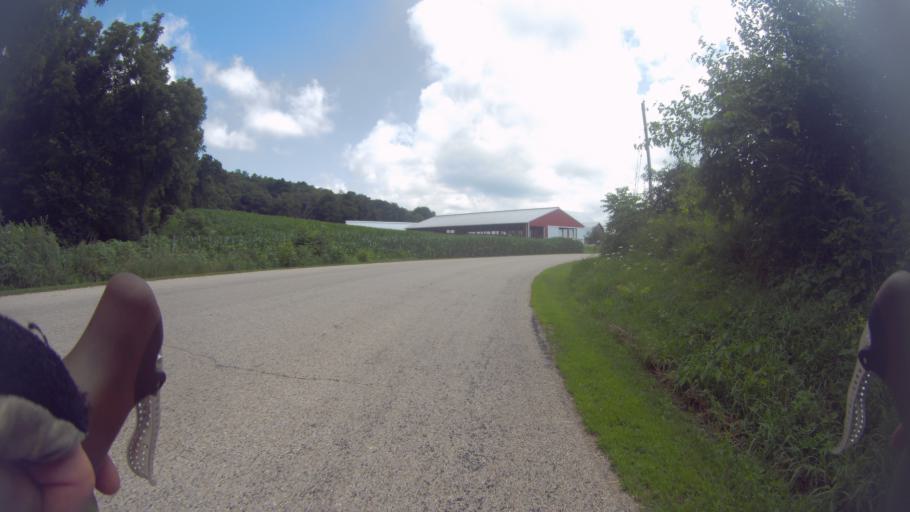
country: US
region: Wisconsin
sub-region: Sauk County
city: Sauk City
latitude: 43.2280
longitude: -89.6202
